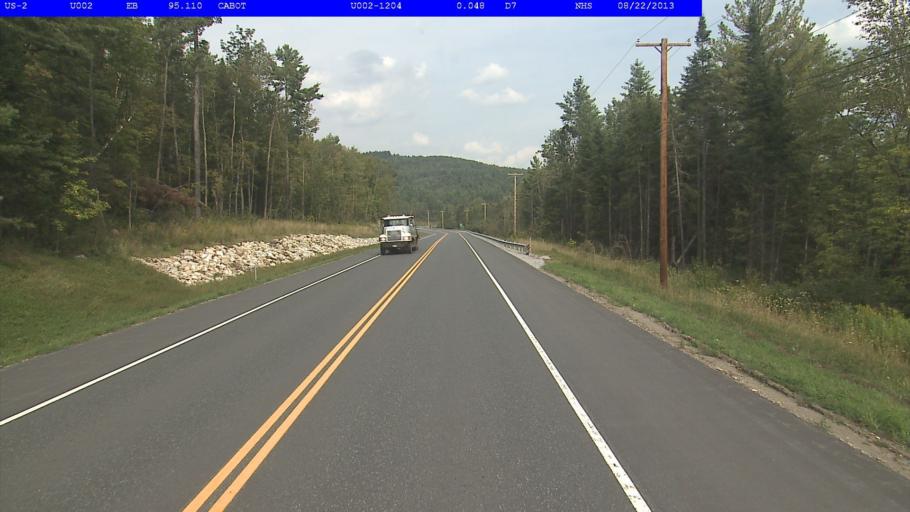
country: US
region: Vermont
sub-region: Caledonia County
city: Hardwick
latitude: 44.3618
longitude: -72.3229
